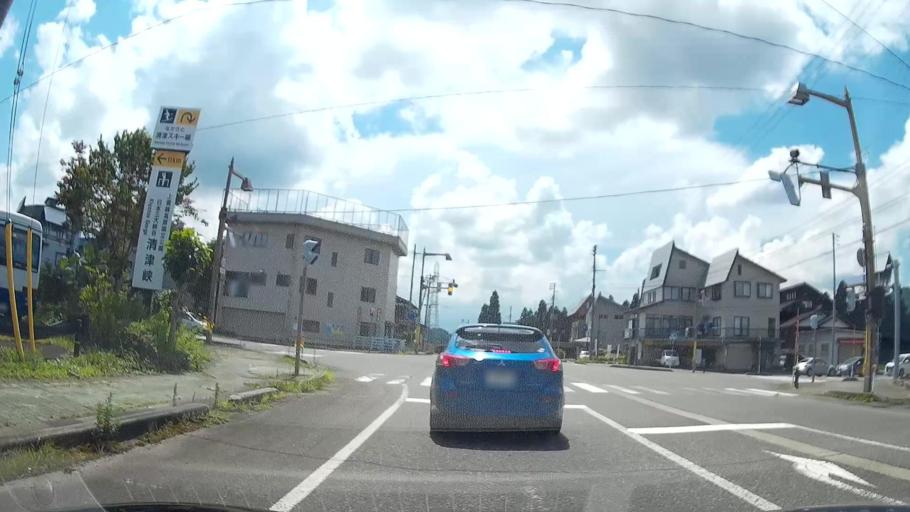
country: JP
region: Niigata
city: Tokamachi
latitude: 37.0513
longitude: 138.6953
